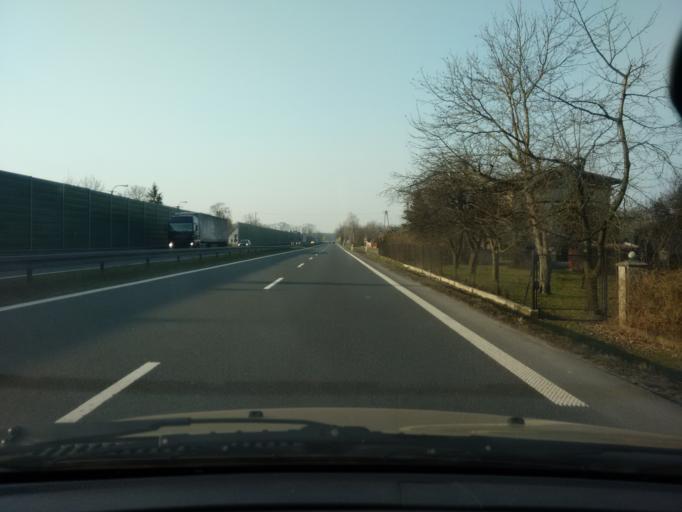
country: PL
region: Silesian Voivodeship
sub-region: Powiat cieszynski
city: Ochaby
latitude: 49.8470
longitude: 18.7633
